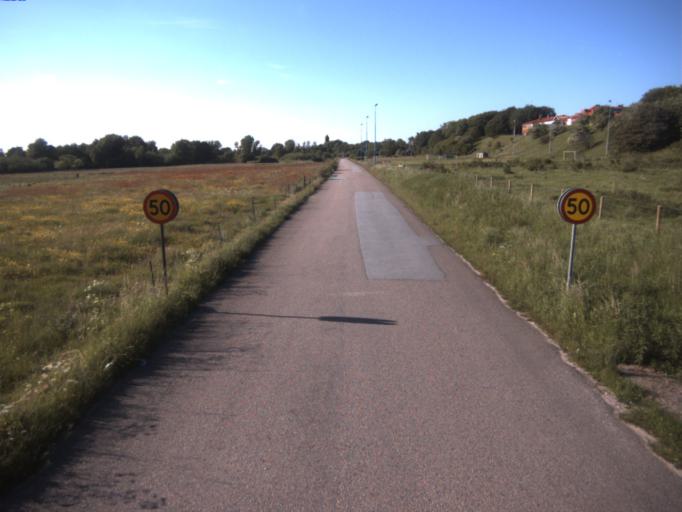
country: SE
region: Skane
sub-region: Helsingborg
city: Rydeback
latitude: 55.9847
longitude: 12.7570
